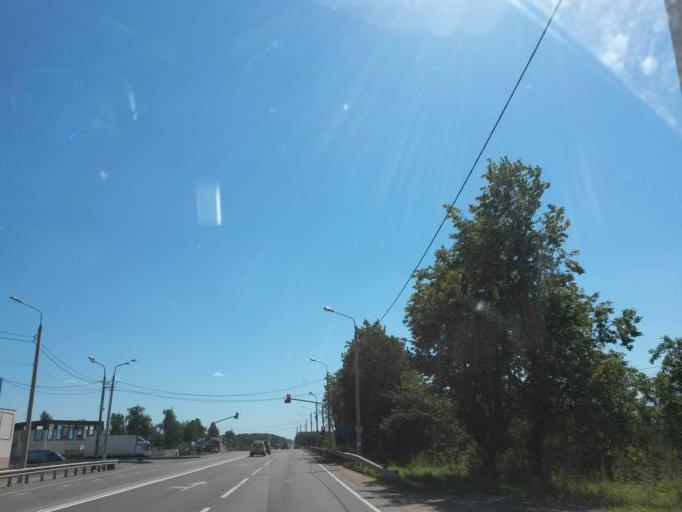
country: RU
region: Moskovskaya
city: Proletarskiy
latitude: 55.0280
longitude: 37.4274
